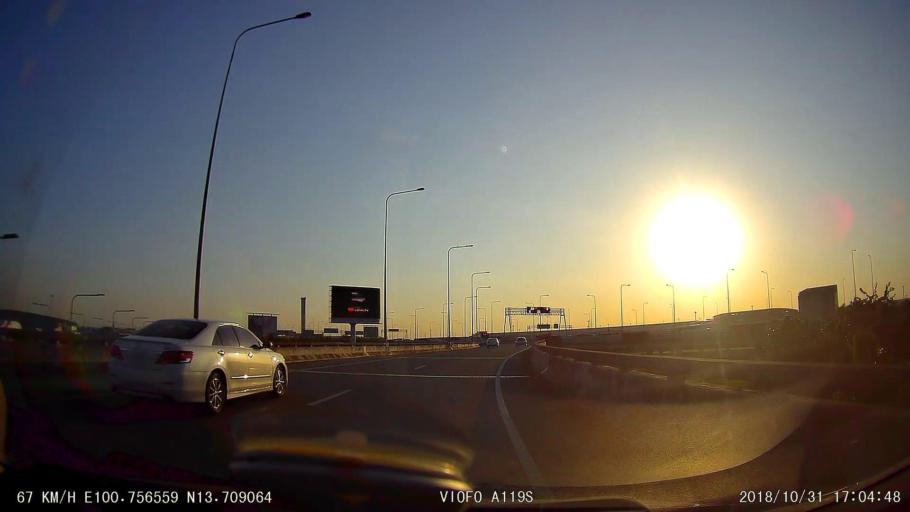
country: TH
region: Bangkok
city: Lat Krabang
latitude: 13.7088
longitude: 100.7567
